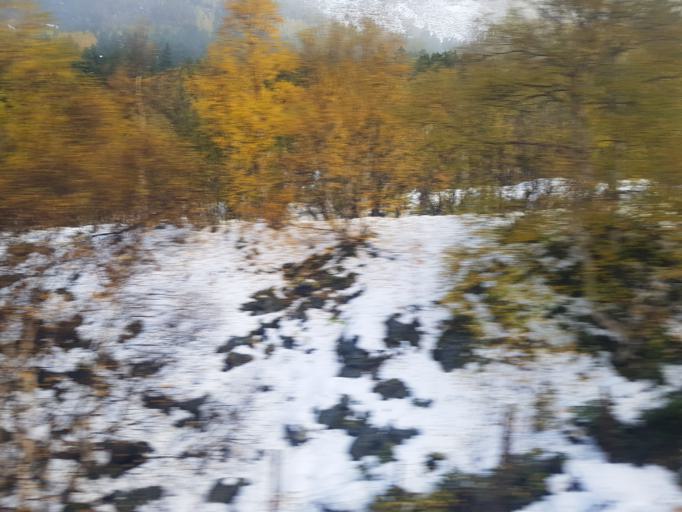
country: NO
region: Sor-Trondelag
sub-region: Oppdal
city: Oppdal
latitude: 62.4315
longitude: 9.6088
